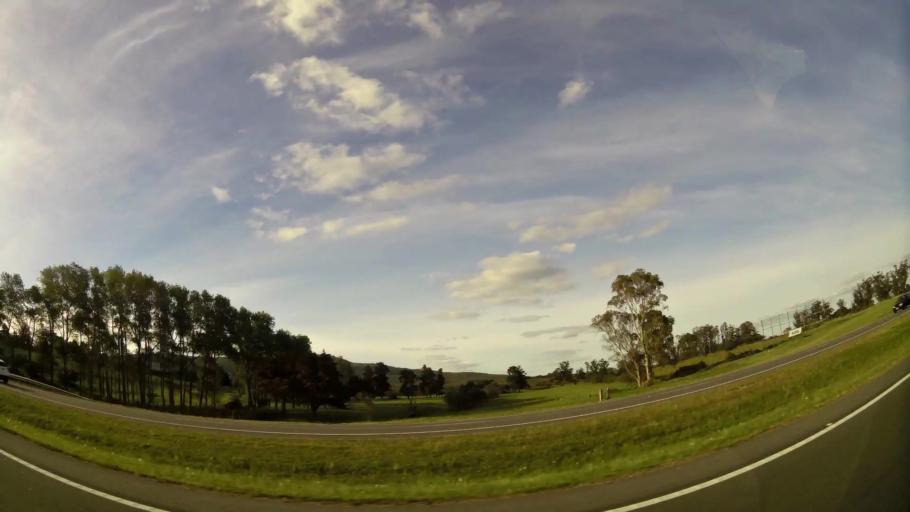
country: UY
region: Maldonado
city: Pan de Azucar
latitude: -34.7897
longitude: -55.3007
